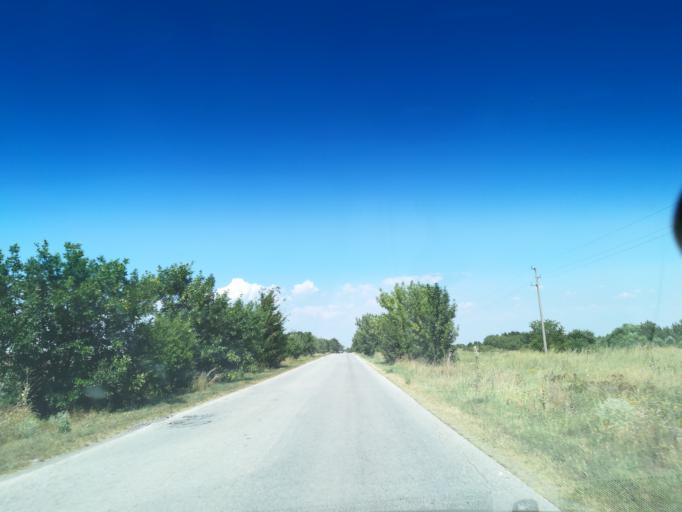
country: BG
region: Plovdiv
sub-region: Obshtina Sadovo
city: Sadovo
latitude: 42.0511
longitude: 25.1470
